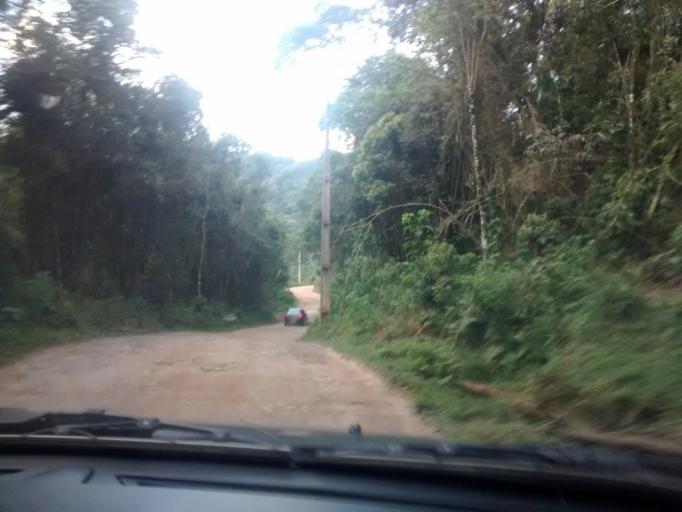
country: BR
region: Sao Paulo
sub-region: Campos Do Jordao
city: Campos do Jordao
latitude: -22.6772
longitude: -45.6319
